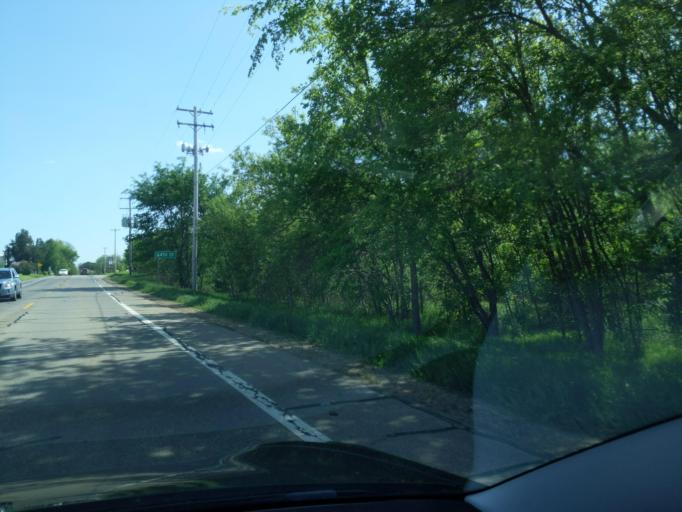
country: US
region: Michigan
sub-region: Kent County
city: Lowell
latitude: 42.8511
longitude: -85.3704
